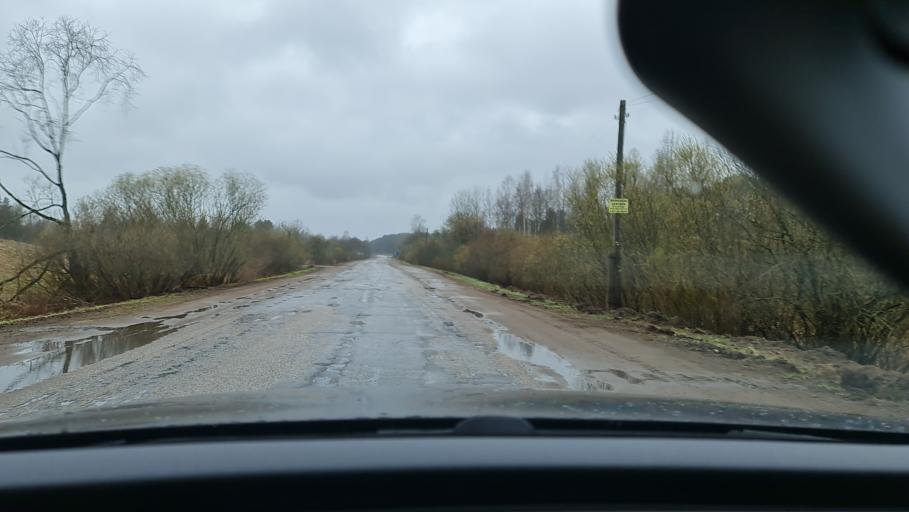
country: RU
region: Novgorod
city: Valday
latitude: 58.0375
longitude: 32.9387
